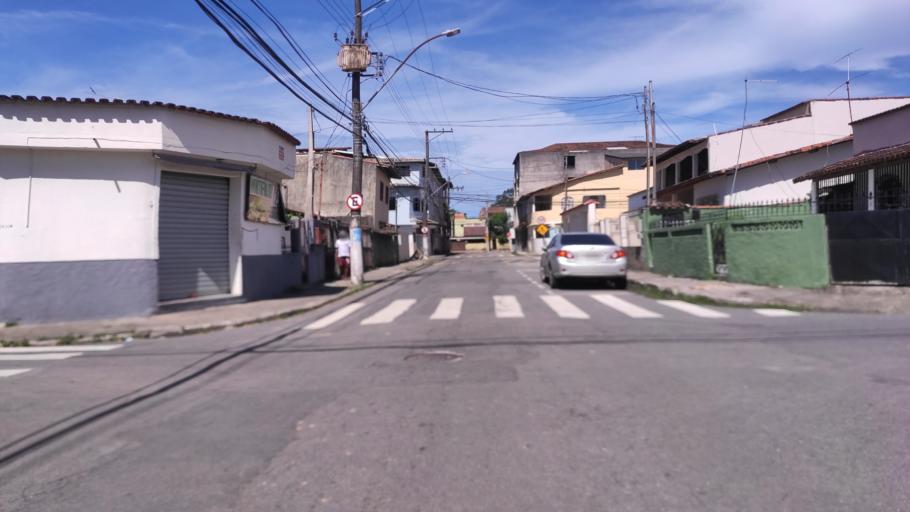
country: BR
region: Espirito Santo
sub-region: Serra
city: Serra
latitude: -20.1942
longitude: -40.2713
